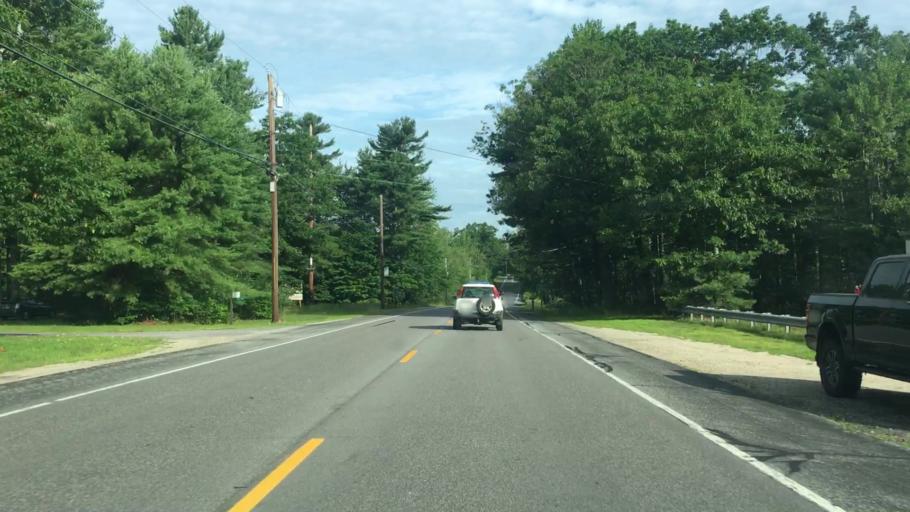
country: US
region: Maine
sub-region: York County
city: Buxton
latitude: 43.7255
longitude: -70.5334
